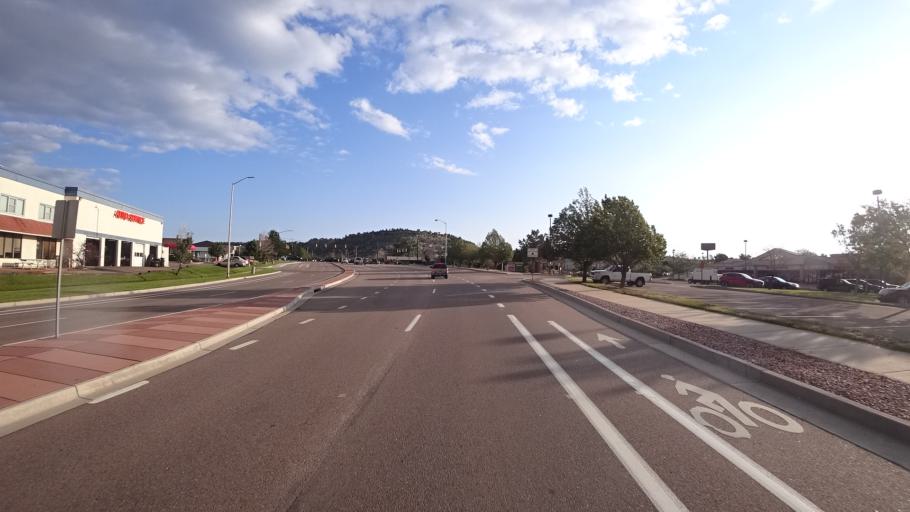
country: US
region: Colorado
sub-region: El Paso County
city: Colorado Springs
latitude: 38.8950
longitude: -104.8512
